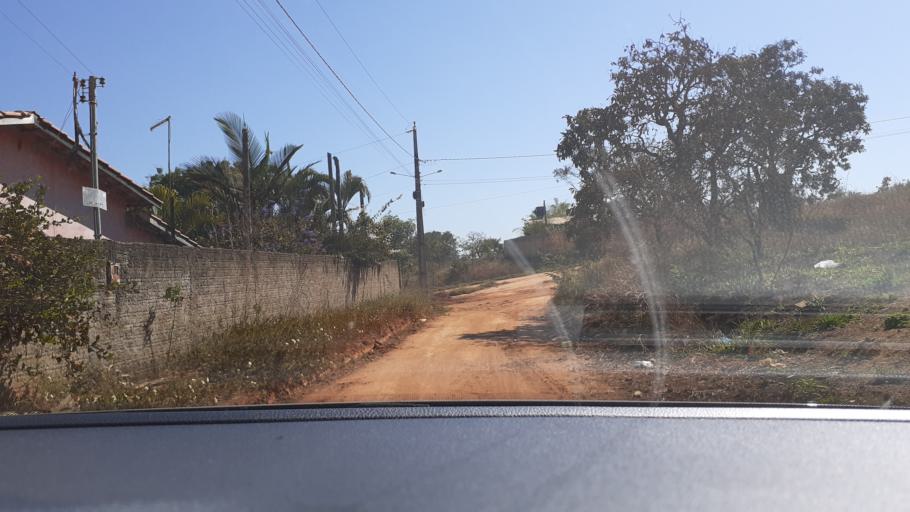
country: BR
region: Goias
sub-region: Aparecida De Goiania
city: Aparecida de Goiania
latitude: -16.8902
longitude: -49.2623
